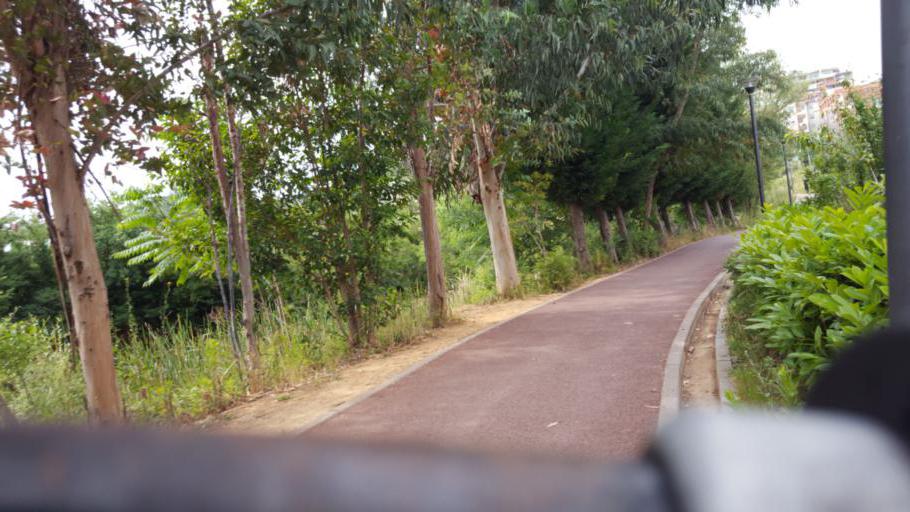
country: AL
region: Tirane
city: Tirana
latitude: 41.3084
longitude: 19.8151
